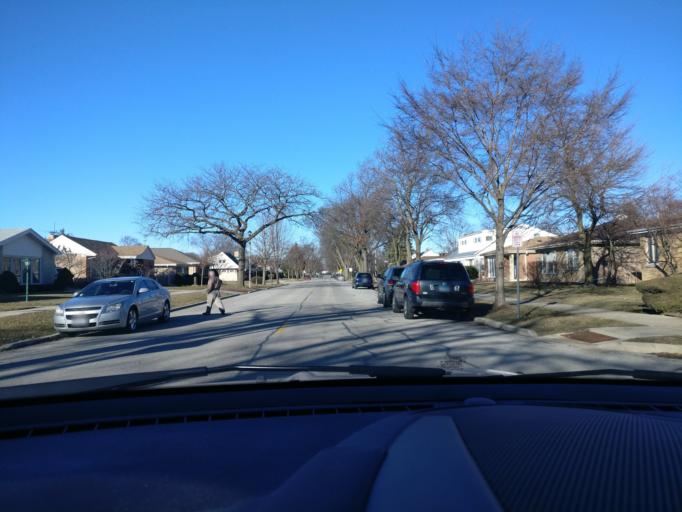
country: US
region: Illinois
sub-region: Cook County
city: Skokie
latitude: 42.0344
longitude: -87.7570
